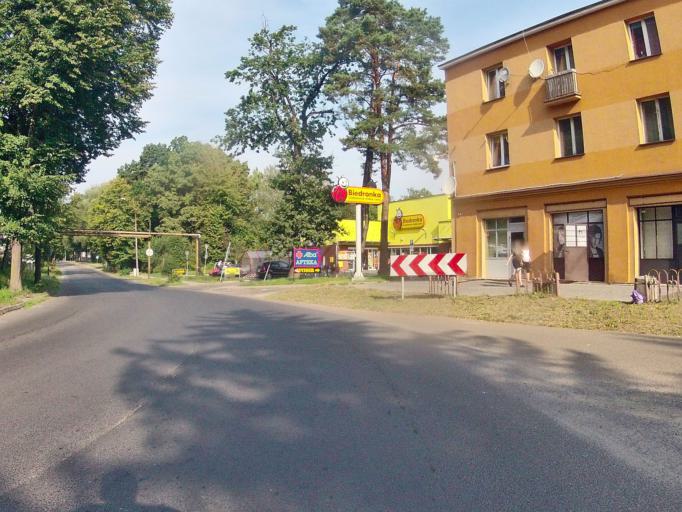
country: PL
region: Subcarpathian Voivodeship
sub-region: Powiat jasielski
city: Trzcinica
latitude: 49.7675
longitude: 21.4206
